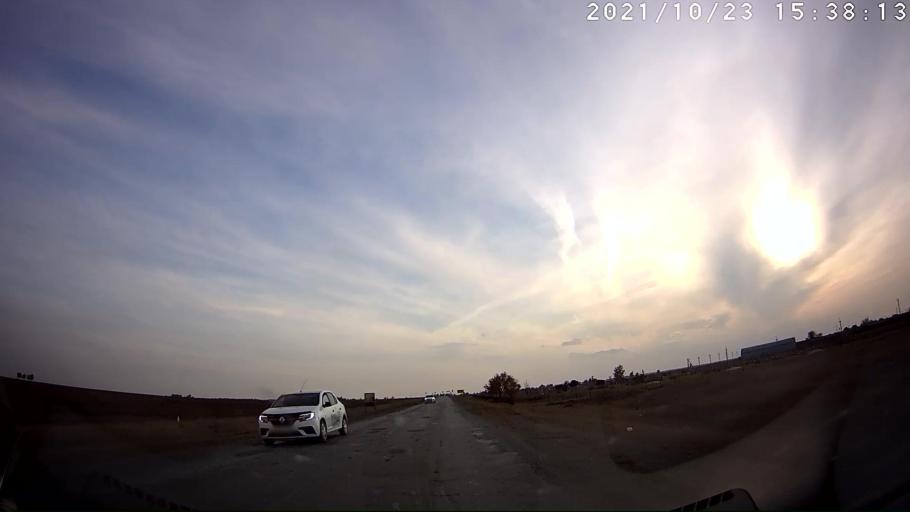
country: RU
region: Volgograd
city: Bereslavka
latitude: 48.1363
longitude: 44.1208
